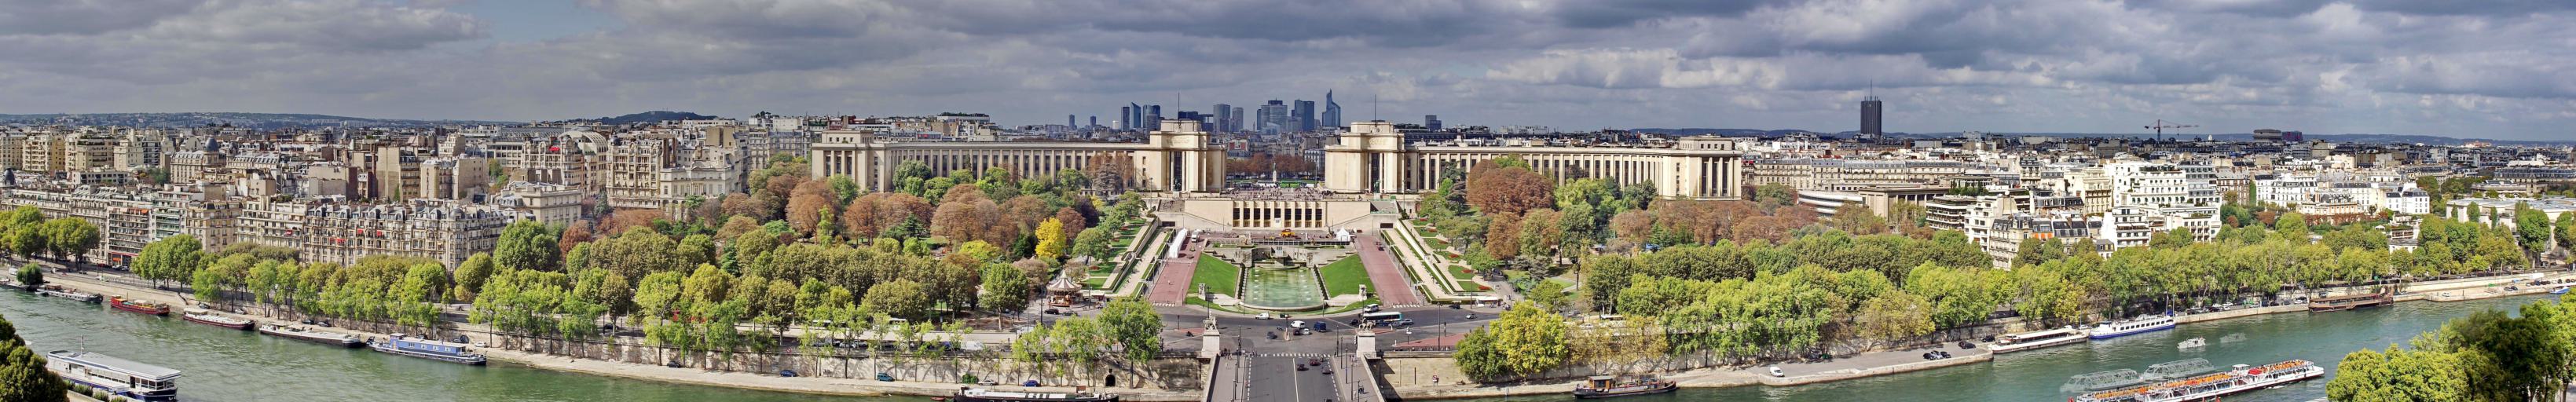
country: FR
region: Ile-de-France
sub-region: Departement des Hauts-de-Seine
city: Vanves
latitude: 48.8580
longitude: 2.2952
